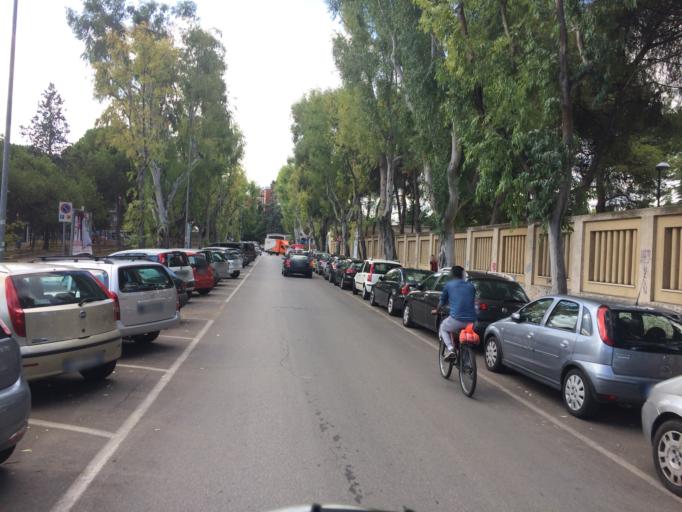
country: IT
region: Apulia
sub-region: Provincia di Bari
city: Bari
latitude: 41.1068
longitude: 16.8598
